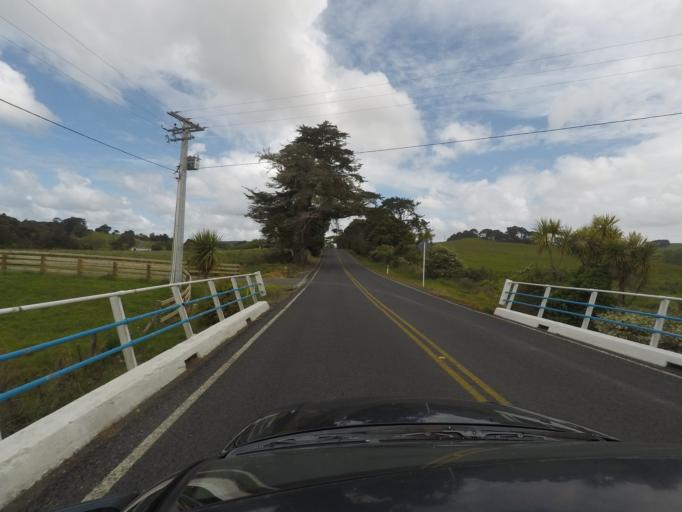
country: NZ
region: Auckland
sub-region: Auckland
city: Parakai
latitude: -36.6497
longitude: 174.5203
